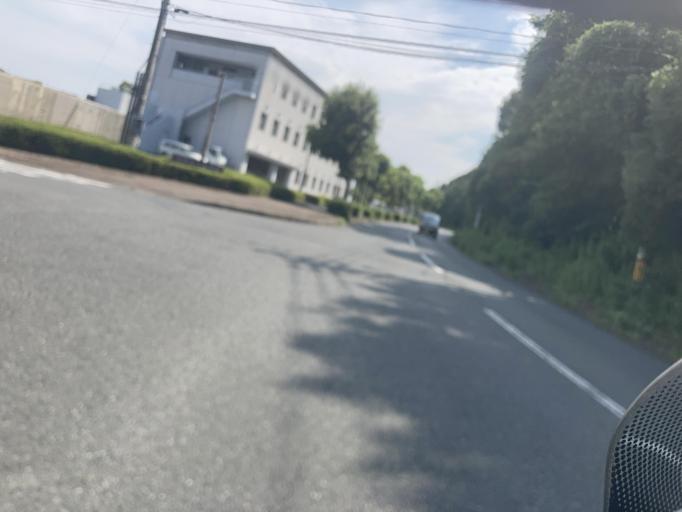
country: JP
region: Fukushima
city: Iwaki
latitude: 37.0169
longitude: 140.9196
